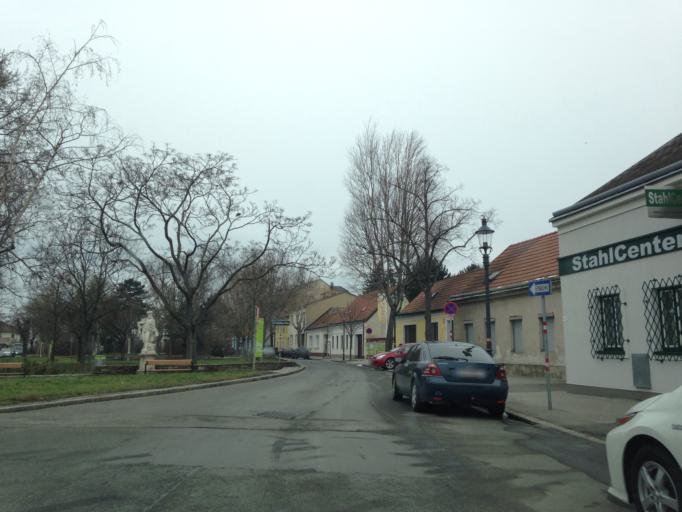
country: AT
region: Lower Austria
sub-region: Politischer Bezirk Wien-Umgebung
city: Gerasdorf bei Wien
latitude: 48.2629
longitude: 16.4451
